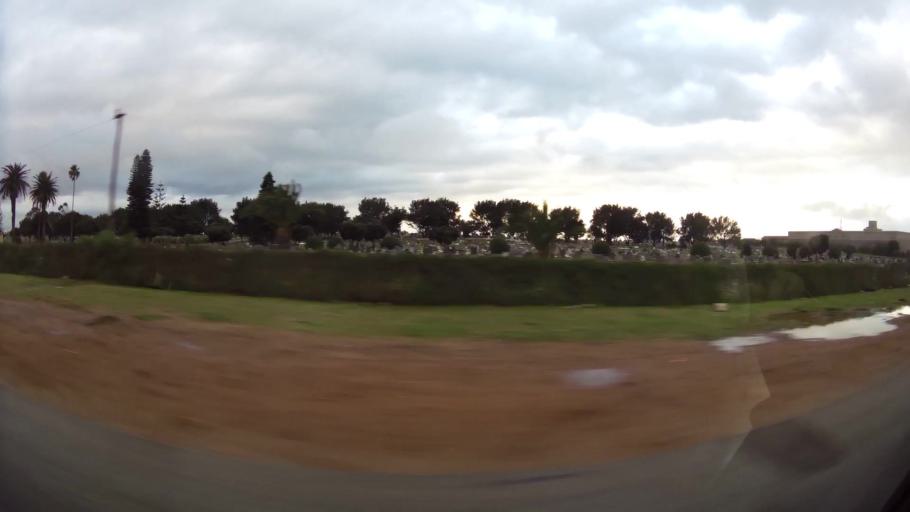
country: ZA
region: Eastern Cape
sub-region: Nelson Mandela Bay Metropolitan Municipality
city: Port Elizabeth
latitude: -33.9255
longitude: 25.6067
